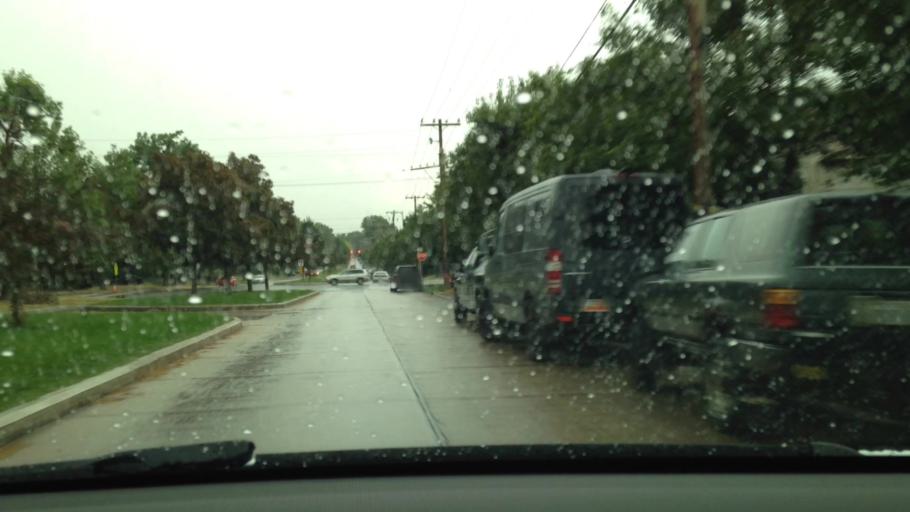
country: US
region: Utah
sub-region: Salt Lake County
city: Salt Lake City
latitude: 40.7572
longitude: -111.8683
